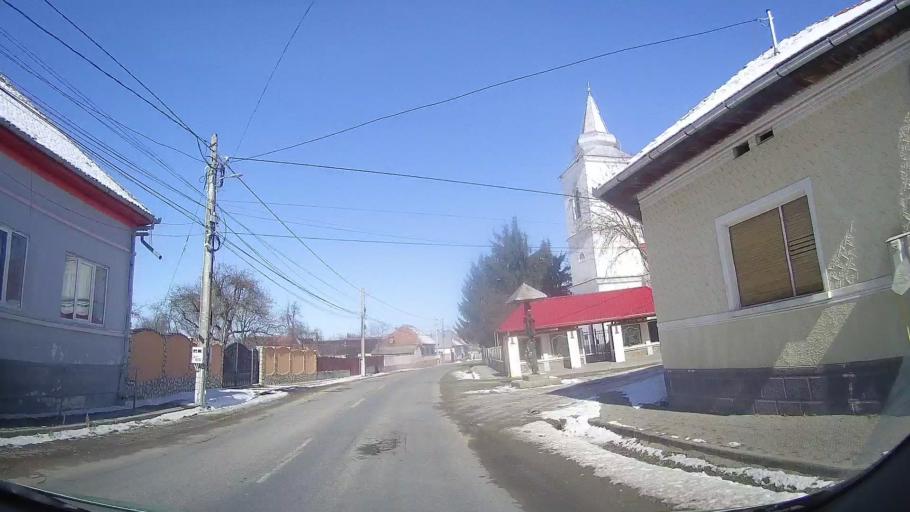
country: RO
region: Brasov
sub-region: Oras Victoria
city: Victoria
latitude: 45.7463
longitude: 24.7396
